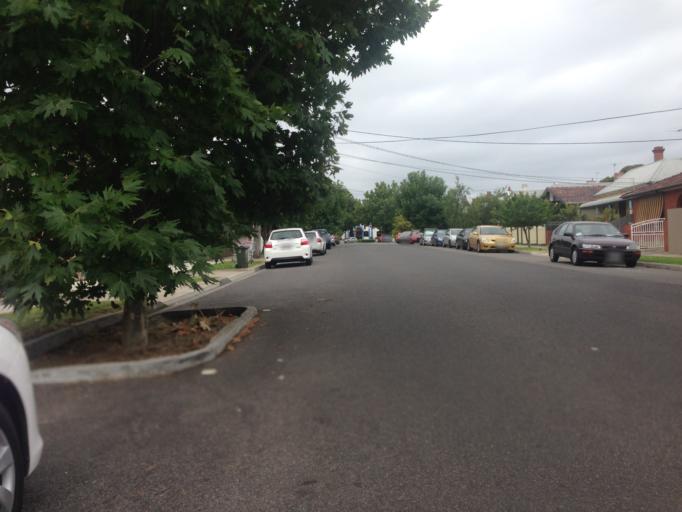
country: AU
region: Victoria
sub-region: Darebin
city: Thornbury
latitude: -37.7613
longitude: 145.0037
